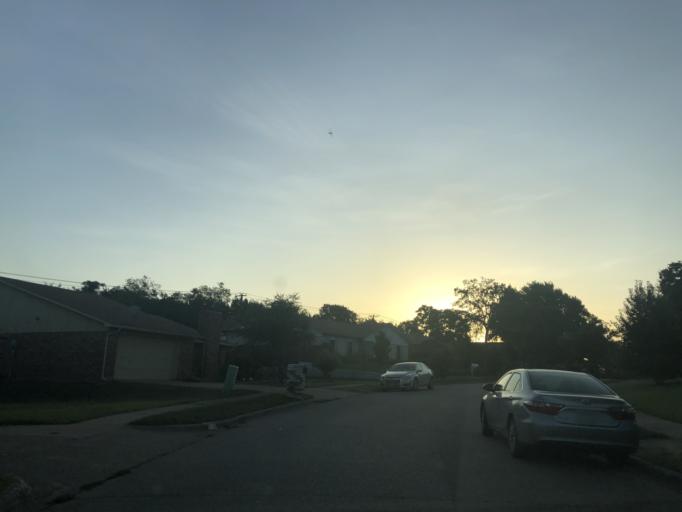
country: US
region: Texas
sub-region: Dallas County
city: Duncanville
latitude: 32.6460
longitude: -96.9580
